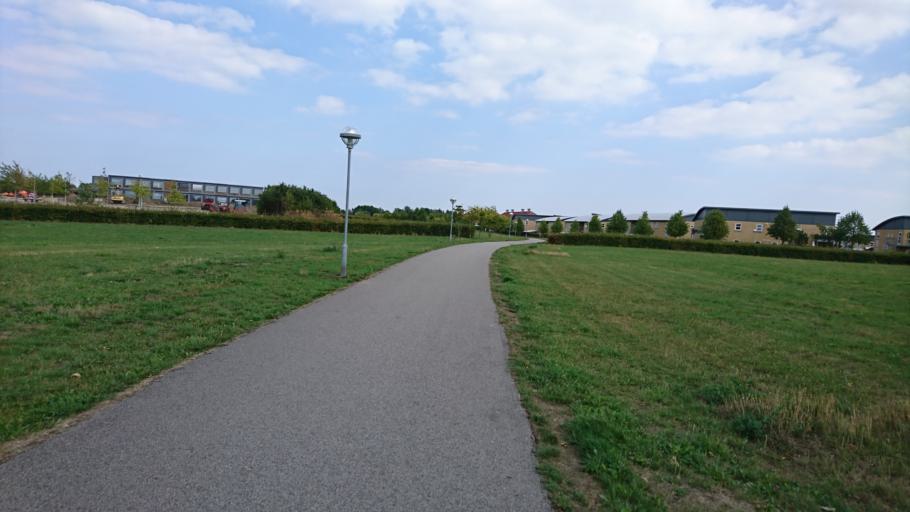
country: DK
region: Capital Region
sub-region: Egedal Kommune
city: Smorumnedre
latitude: 55.7476
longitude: 12.2908
